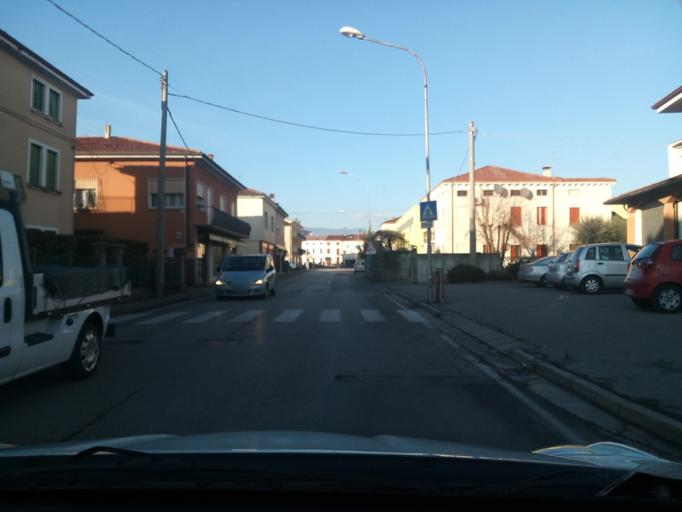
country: IT
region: Veneto
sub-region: Provincia di Vicenza
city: Dueville
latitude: 45.6344
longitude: 11.5507
